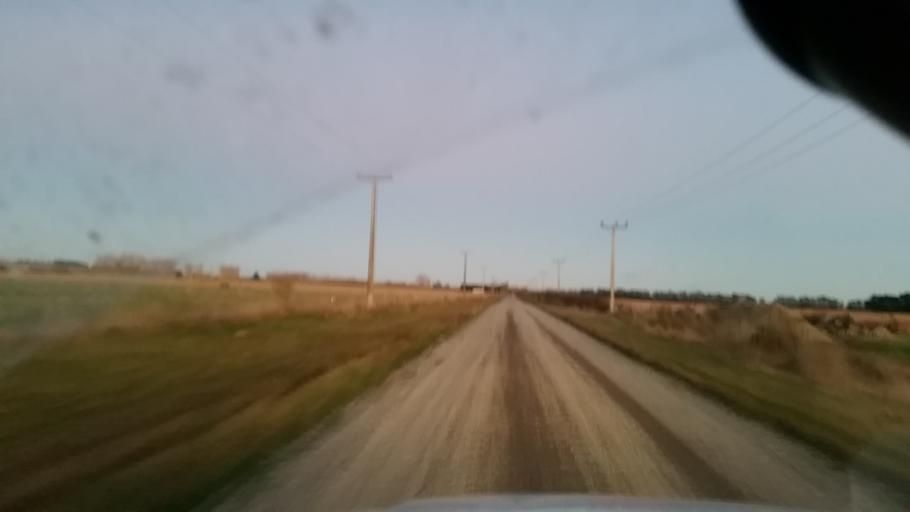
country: NZ
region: Canterbury
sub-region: Ashburton District
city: Tinwald
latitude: -43.9919
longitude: 171.6587
